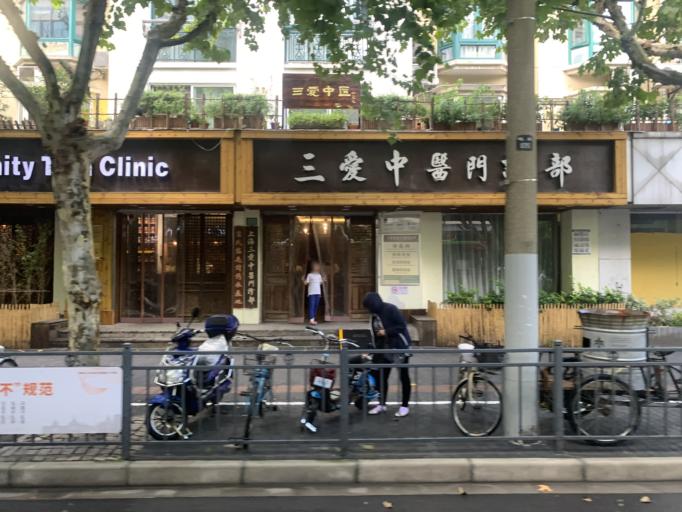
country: CN
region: Shanghai Shi
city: Luwan
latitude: 31.2145
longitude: 121.4724
